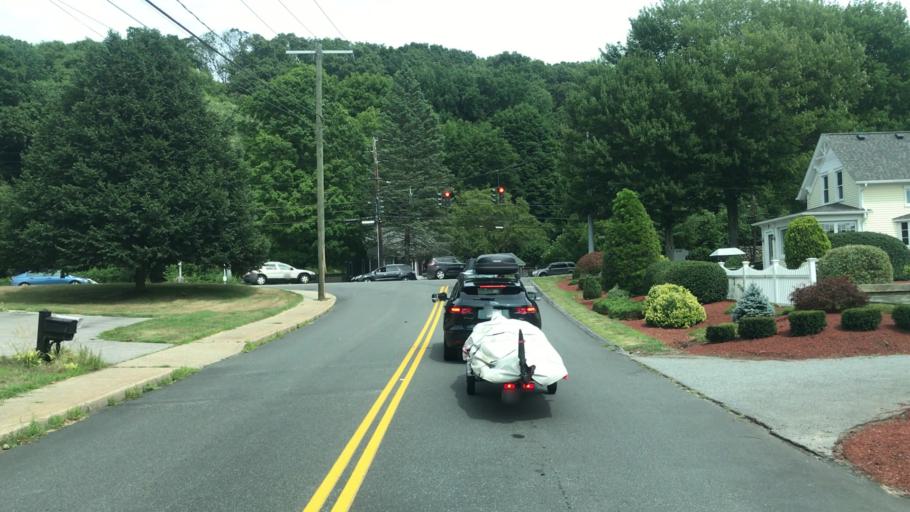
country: US
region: Connecticut
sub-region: New London County
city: Niantic
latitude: 41.3467
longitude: -72.2105
